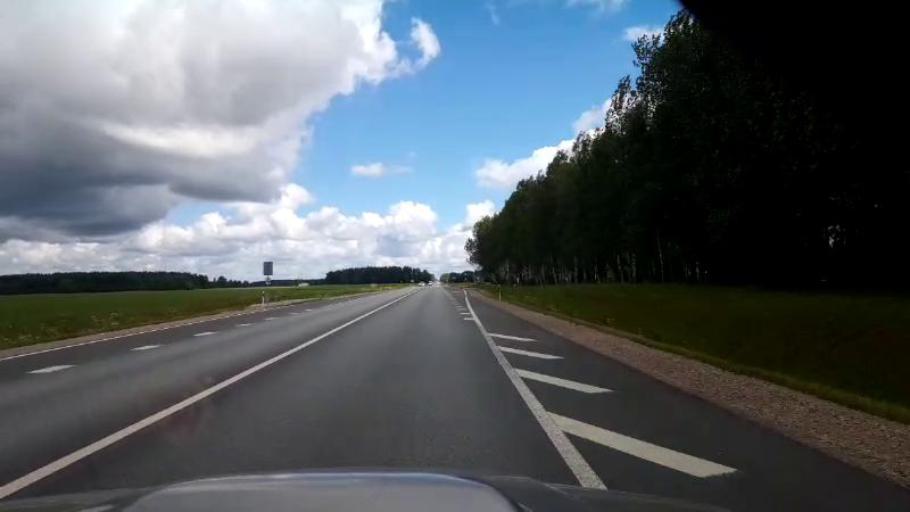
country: LV
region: Lecava
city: Iecava
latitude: 56.6453
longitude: 24.2278
